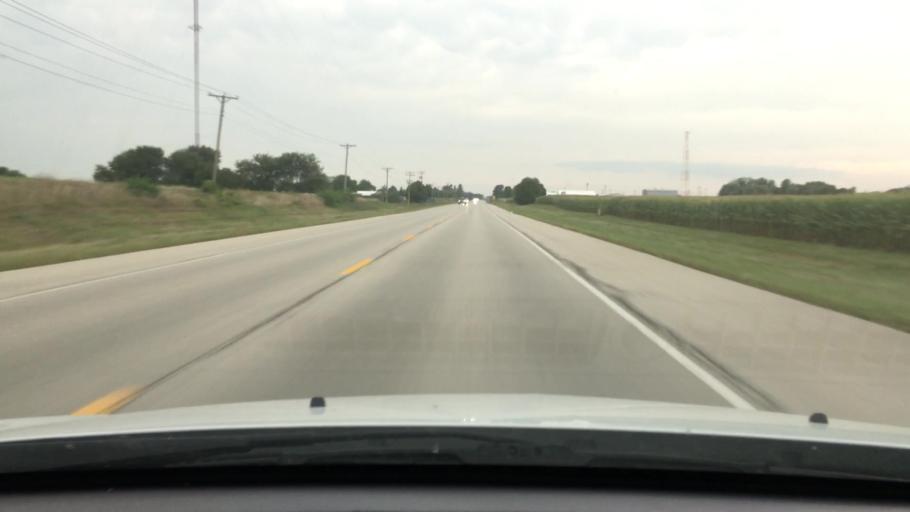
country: US
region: Illinois
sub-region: DeKalb County
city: DeKalb
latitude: 41.8730
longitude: -88.7538
